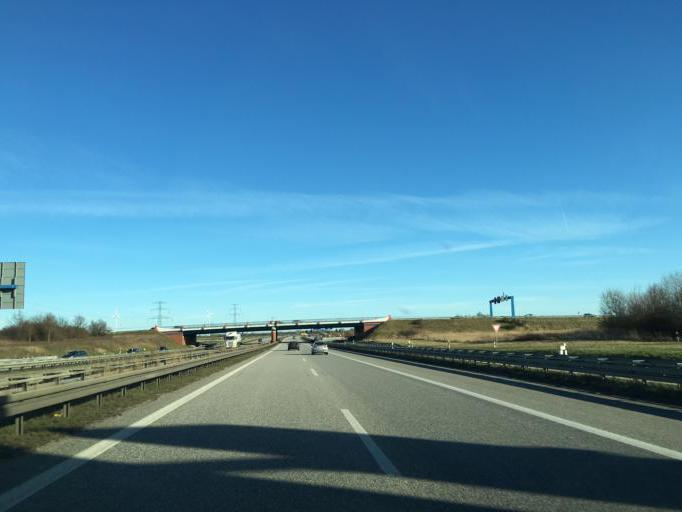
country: DE
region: Mecklenburg-Vorpommern
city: Dierkow-Neu
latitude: 54.1085
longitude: 12.1863
